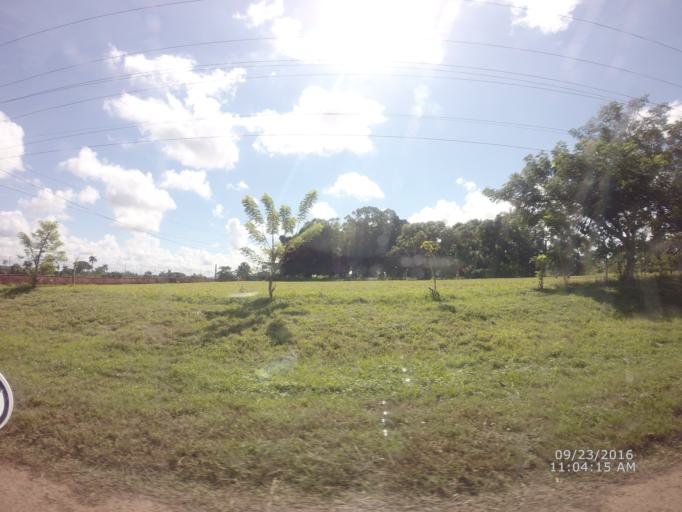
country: CU
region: Mayabeque
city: Jamaica
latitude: 23.0007
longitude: -82.2180
